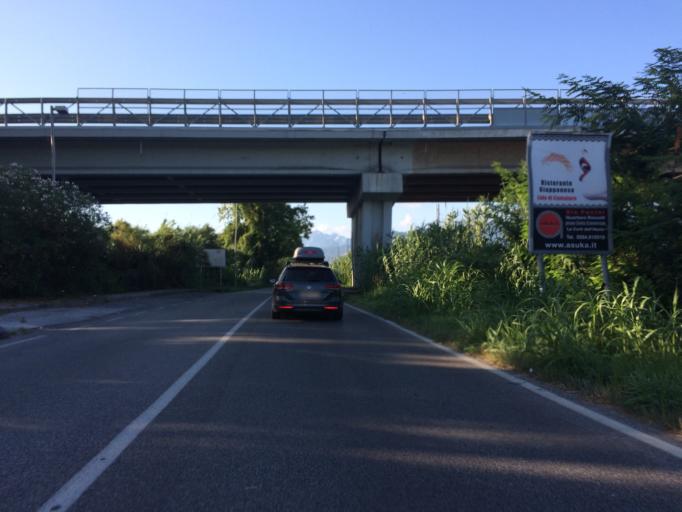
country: IT
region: Tuscany
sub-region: Provincia di Lucca
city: Viareggio
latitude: 43.8883
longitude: 10.2502
